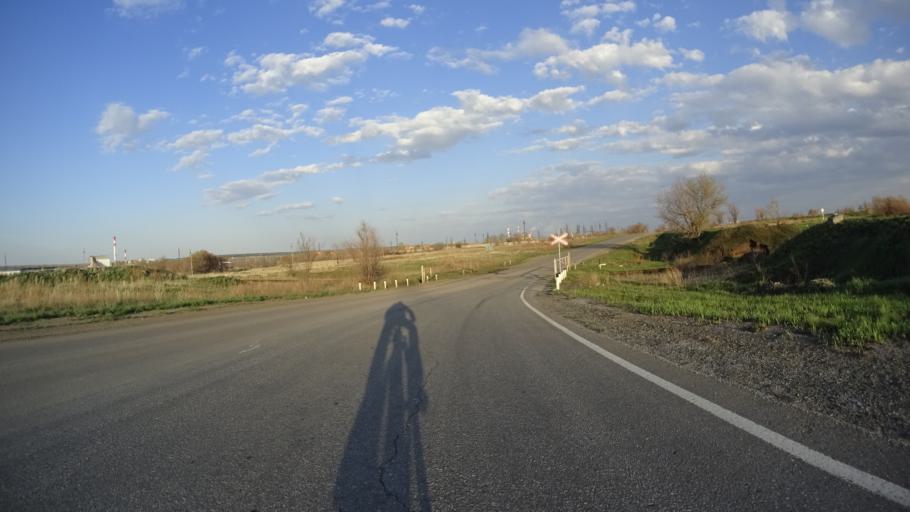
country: RU
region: Chelyabinsk
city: Troitsk
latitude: 54.0623
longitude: 61.5752
